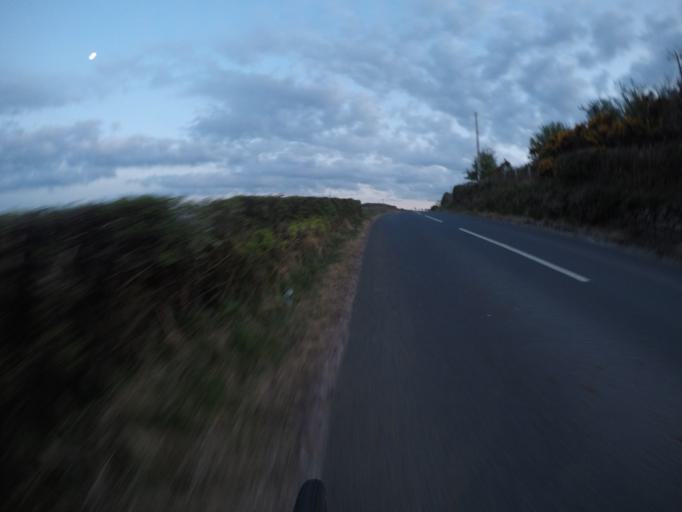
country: GB
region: Scotland
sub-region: South Ayrshire
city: Dundonald
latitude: 55.5666
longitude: -4.6014
